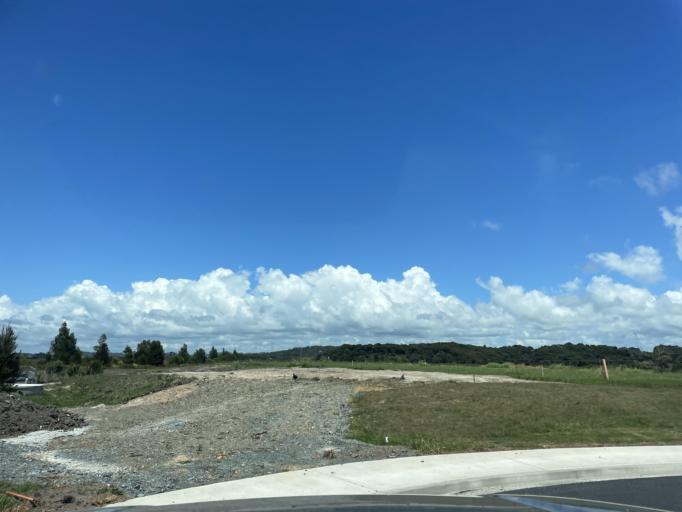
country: NZ
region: Auckland
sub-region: Auckland
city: Wellsford
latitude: -36.0927
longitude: 174.5722
